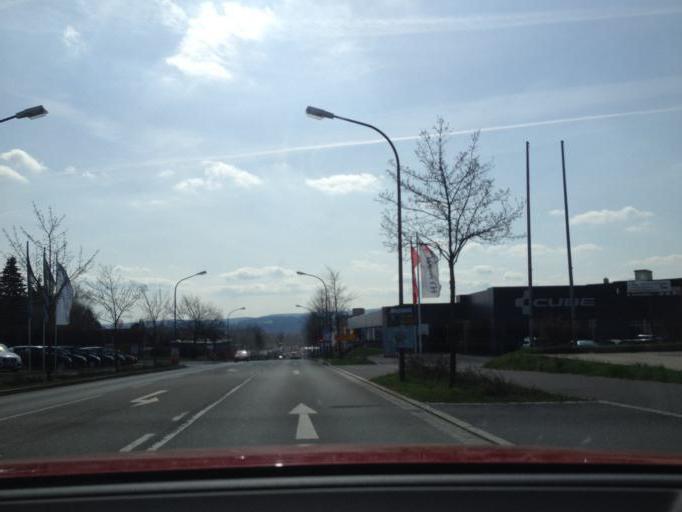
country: DE
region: Bavaria
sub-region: Upper Franconia
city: Marktredwitz
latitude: 50.0080
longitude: 12.0775
